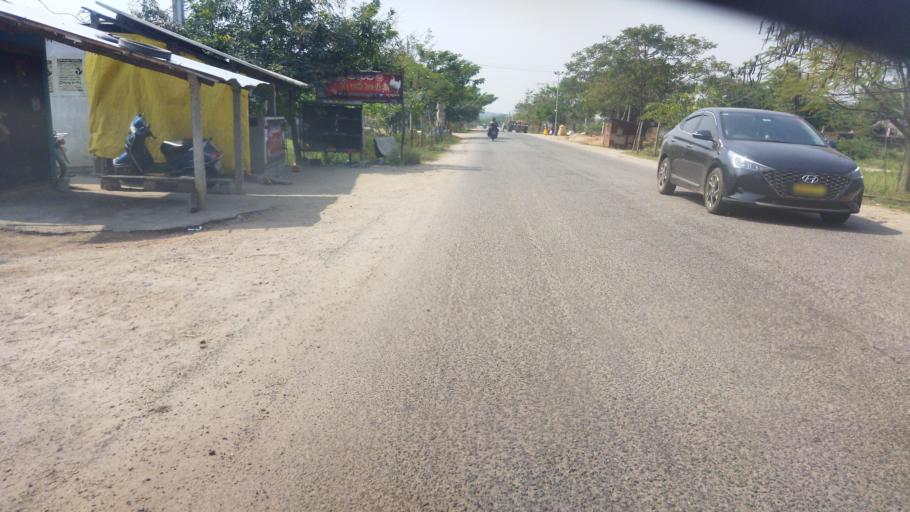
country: IN
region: Telangana
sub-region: Nalgonda
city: Nalgonda
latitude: 17.1197
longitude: 79.2864
